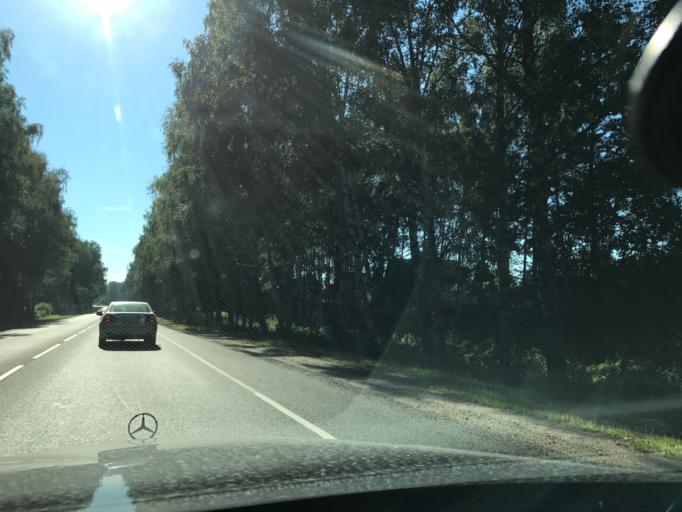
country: RU
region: Moskovskaya
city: Noginsk-9
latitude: 56.1009
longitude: 38.6567
